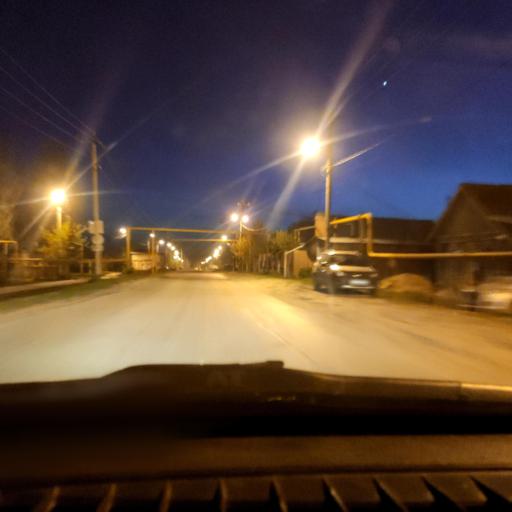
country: RU
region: Samara
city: Zhigulevsk
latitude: 53.4672
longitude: 49.6326
